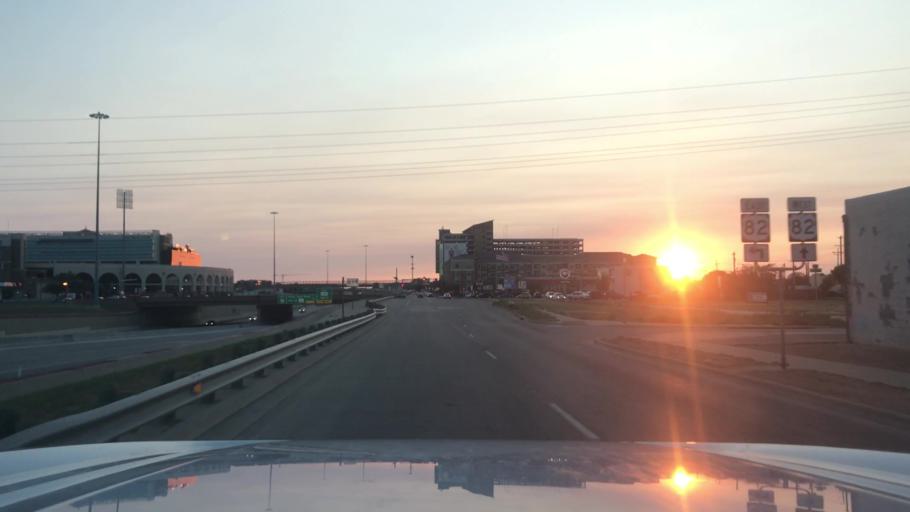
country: US
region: Texas
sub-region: Lubbock County
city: Lubbock
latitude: 33.5931
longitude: -101.8679
